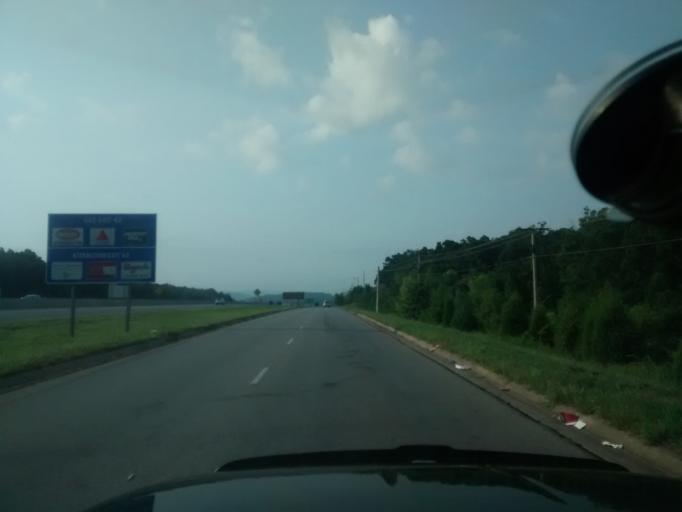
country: US
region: Arkansas
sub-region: Washington County
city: Fayetteville
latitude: 36.0662
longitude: -94.2015
